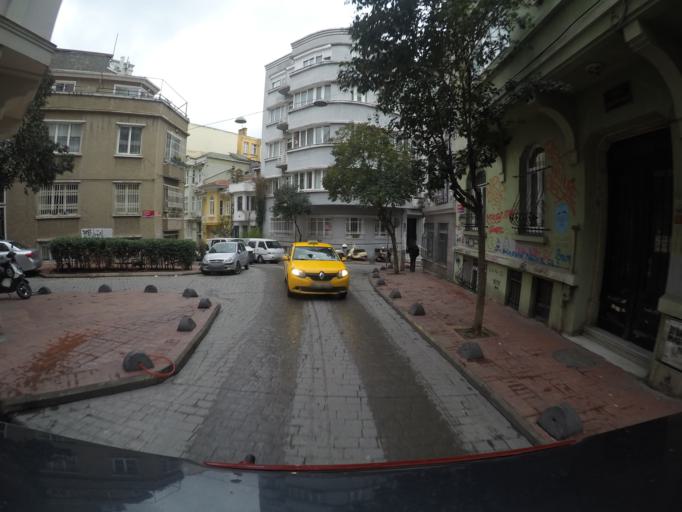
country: TR
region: Istanbul
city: Eminoenue
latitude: 41.0313
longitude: 28.9851
